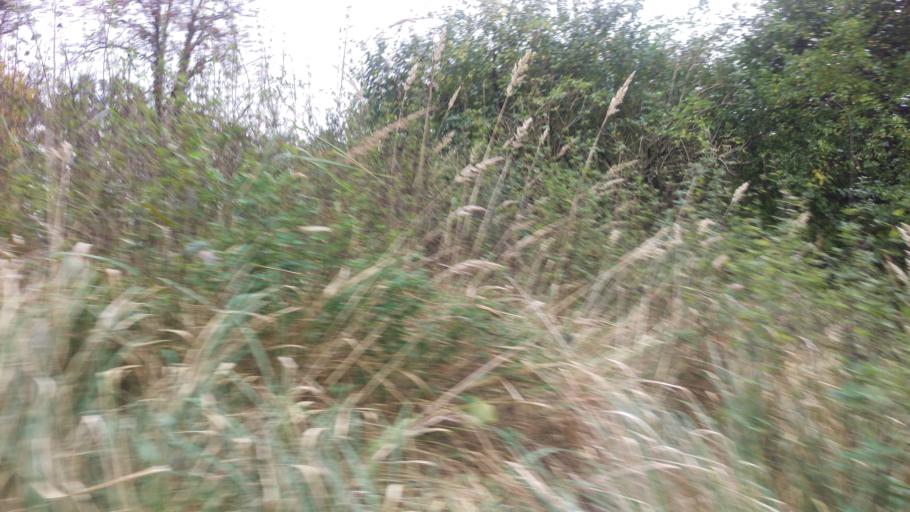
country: PL
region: West Pomeranian Voivodeship
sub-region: Szczecin
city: Szczecin
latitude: 53.3942
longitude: 14.6767
